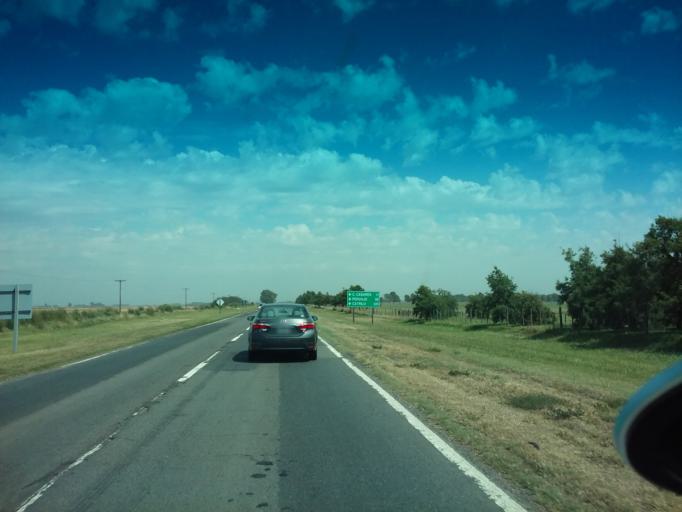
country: AR
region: Buenos Aires
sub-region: Partido de Carlos Casares
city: Carlos Casares
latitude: -35.6147
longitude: -61.2665
